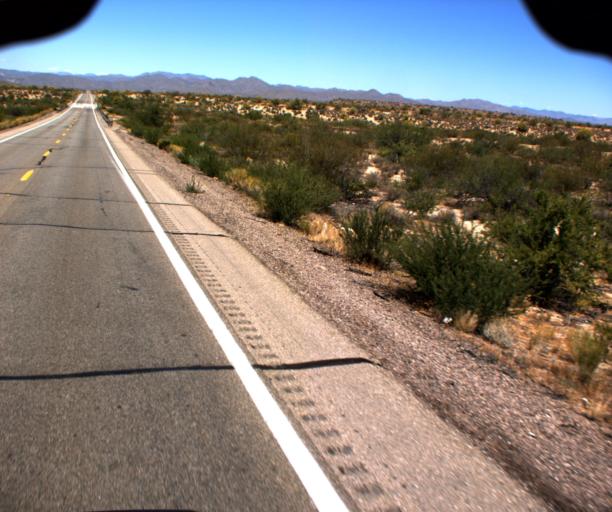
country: US
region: Arizona
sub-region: Yavapai County
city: Bagdad
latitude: 34.3149
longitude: -113.1302
